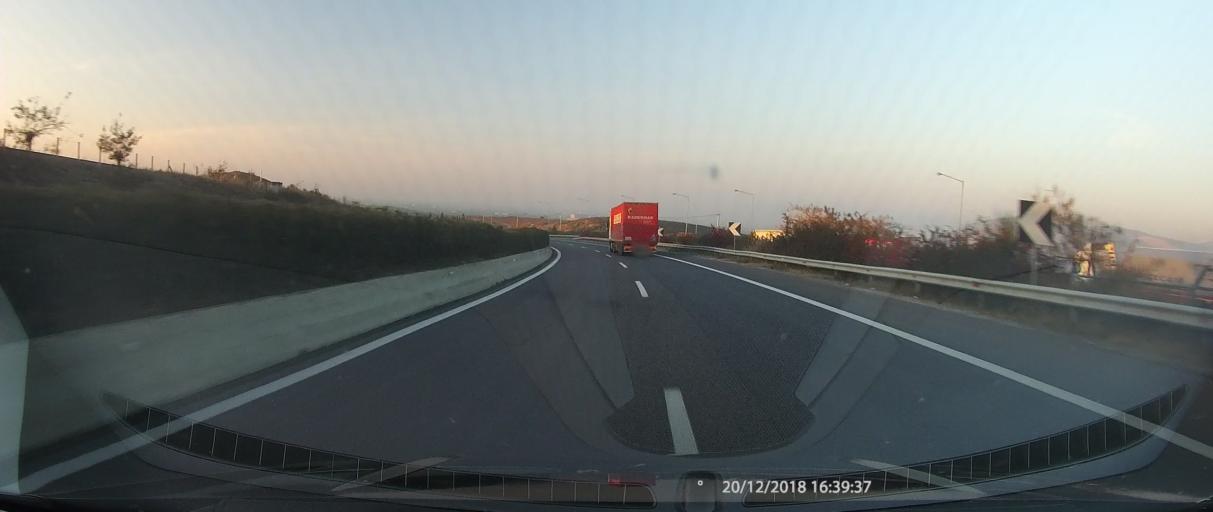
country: GR
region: Thessaly
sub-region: Nomos Magnisias
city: Velestino
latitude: 39.3613
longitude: 22.7738
